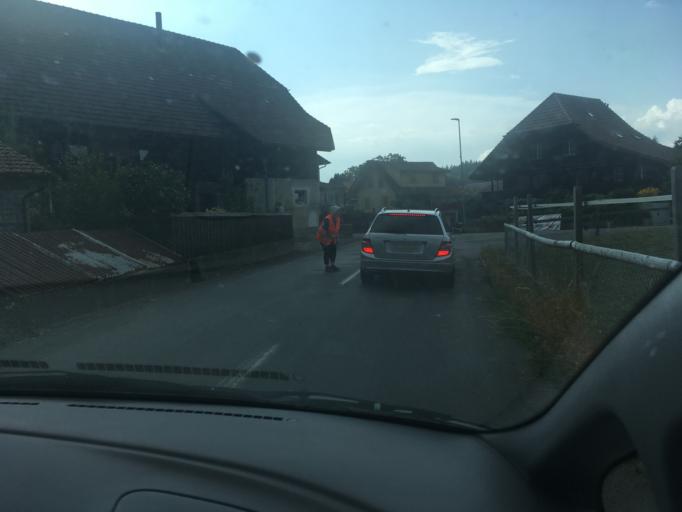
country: CH
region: Bern
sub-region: Bern-Mittelland District
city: Wohlen
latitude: 47.0038
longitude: 7.3370
